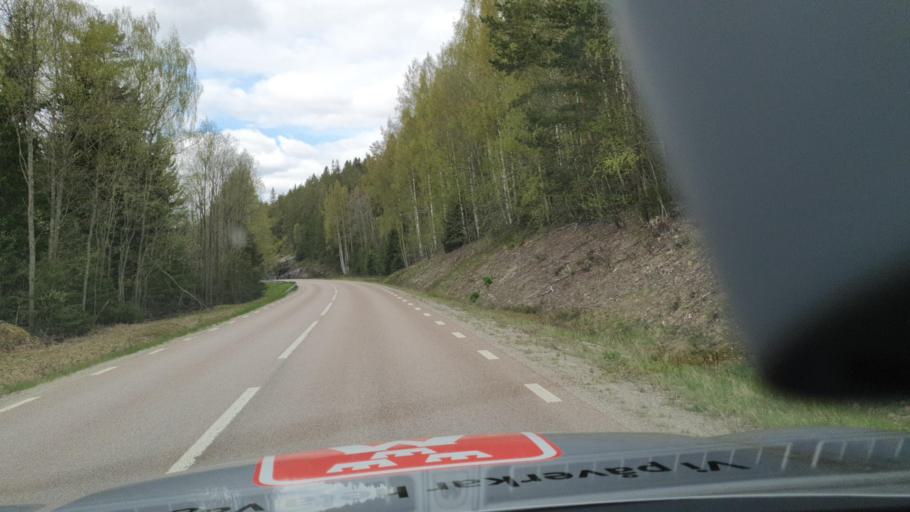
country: SE
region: Vaesternorrland
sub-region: OErnskoeldsviks Kommun
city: Ornskoldsvik
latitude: 63.5174
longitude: 18.7514
